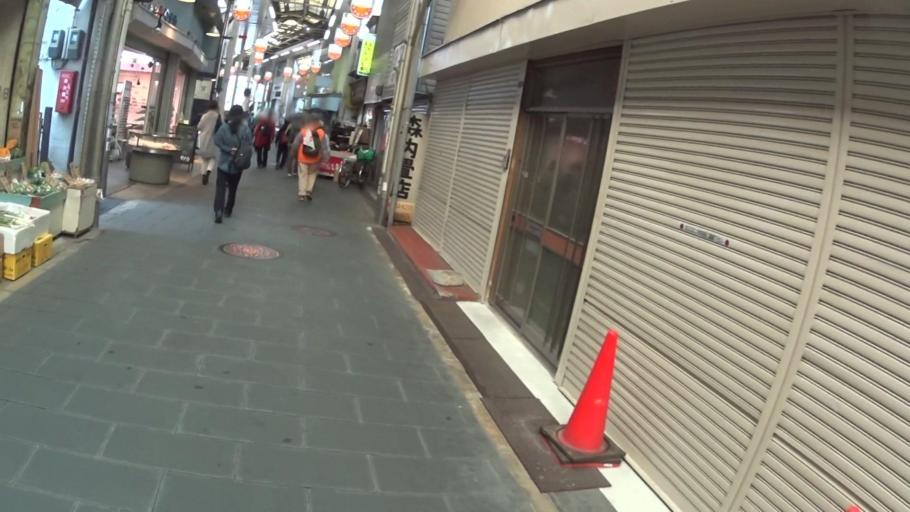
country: JP
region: Osaka
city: Kashihara
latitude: 34.5707
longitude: 135.5959
